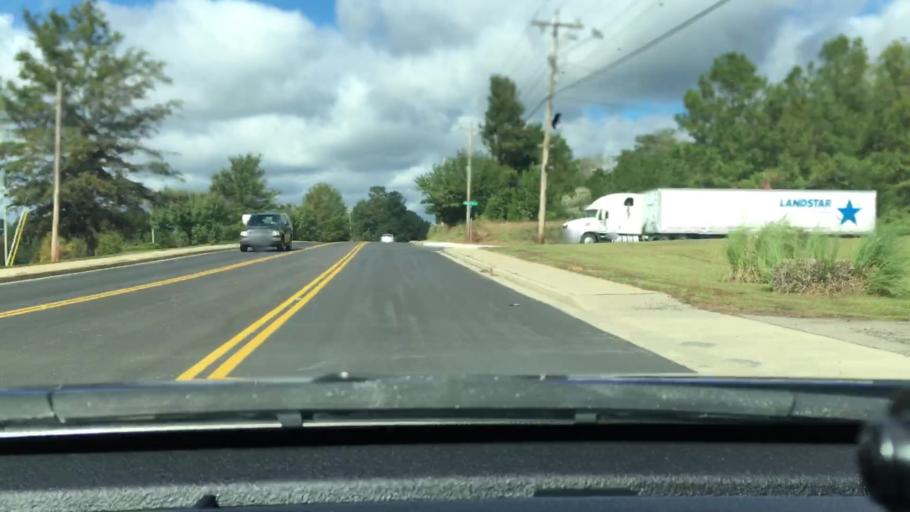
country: US
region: South Carolina
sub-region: Lexington County
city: Irmo
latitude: 34.1165
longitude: -81.1673
